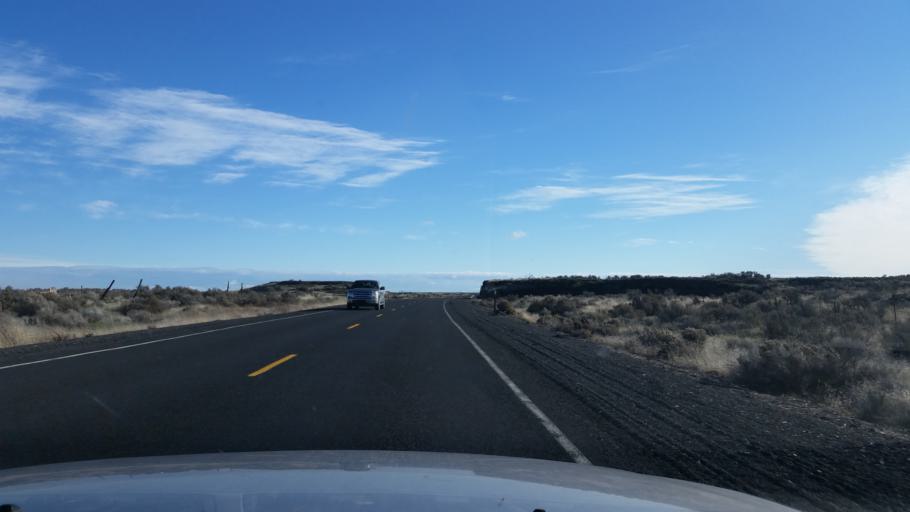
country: US
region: Washington
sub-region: Grant County
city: Warden
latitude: 47.3283
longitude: -118.8740
